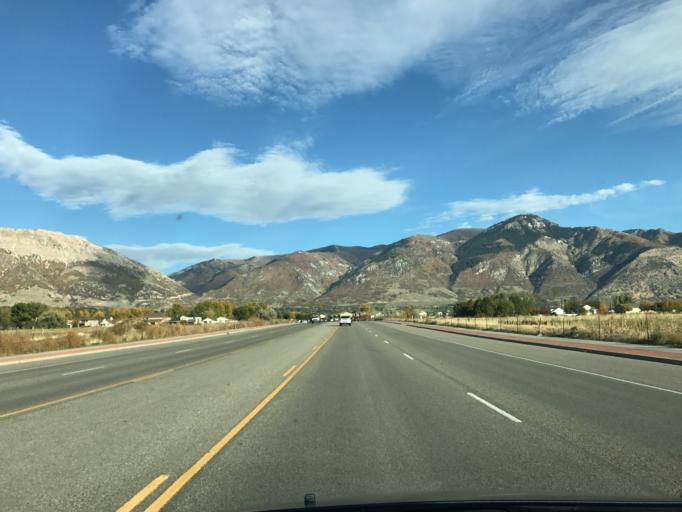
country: US
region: Utah
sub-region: Weber County
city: Pleasant View
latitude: 41.3060
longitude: -111.9903
